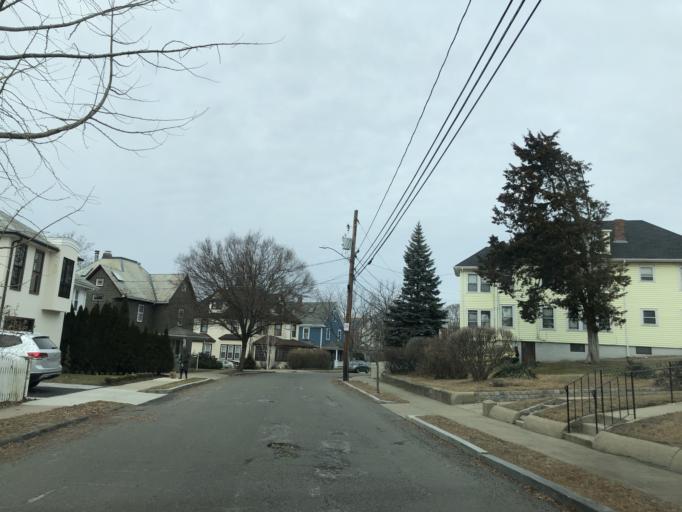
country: US
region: Massachusetts
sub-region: Middlesex County
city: Watertown
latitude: 42.3666
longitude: -71.1702
